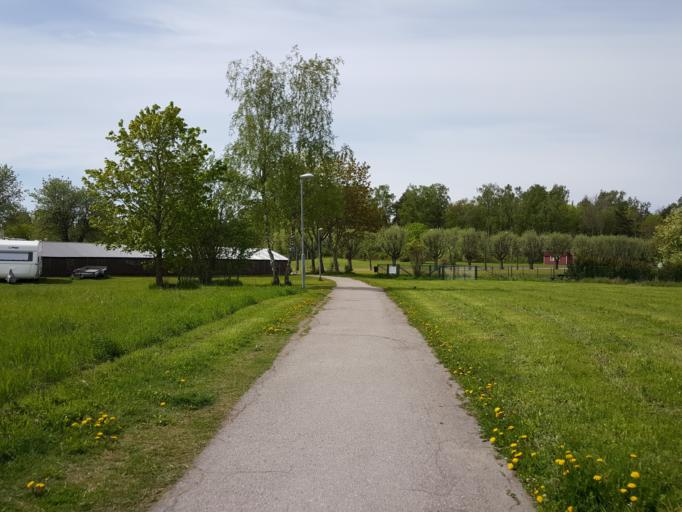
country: SE
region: Uppsala
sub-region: Osthammars Kommun
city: Gimo
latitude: 60.1757
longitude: 18.1840
